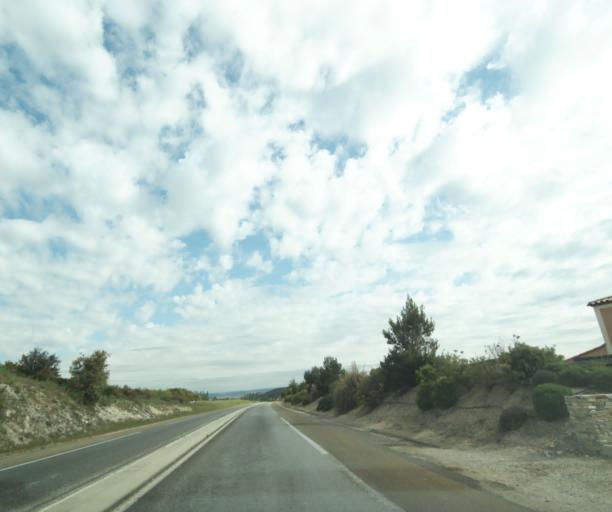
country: FR
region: Provence-Alpes-Cote d'Azur
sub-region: Departement des Bouches-du-Rhone
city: Cabries
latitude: 43.4672
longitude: 5.3541
